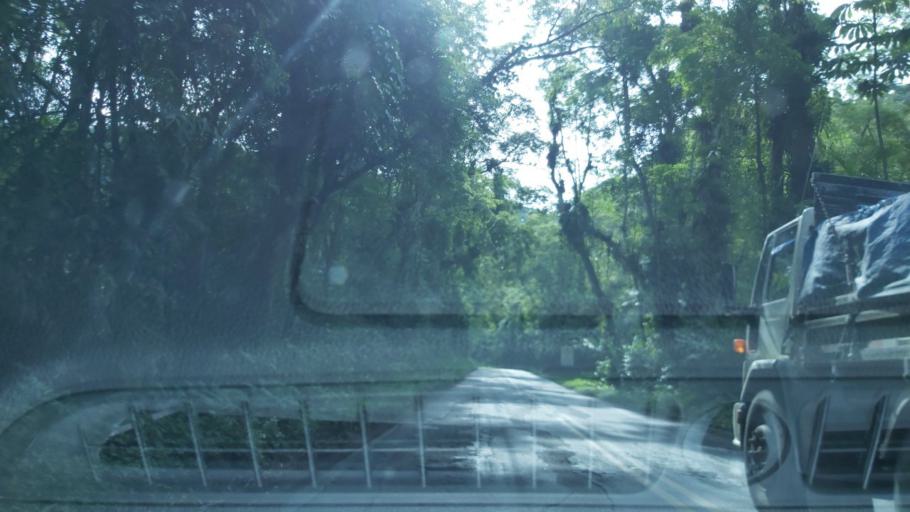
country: BR
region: Sao Paulo
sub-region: Miracatu
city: Miracatu
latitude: -24.0541
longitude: -47.5725
